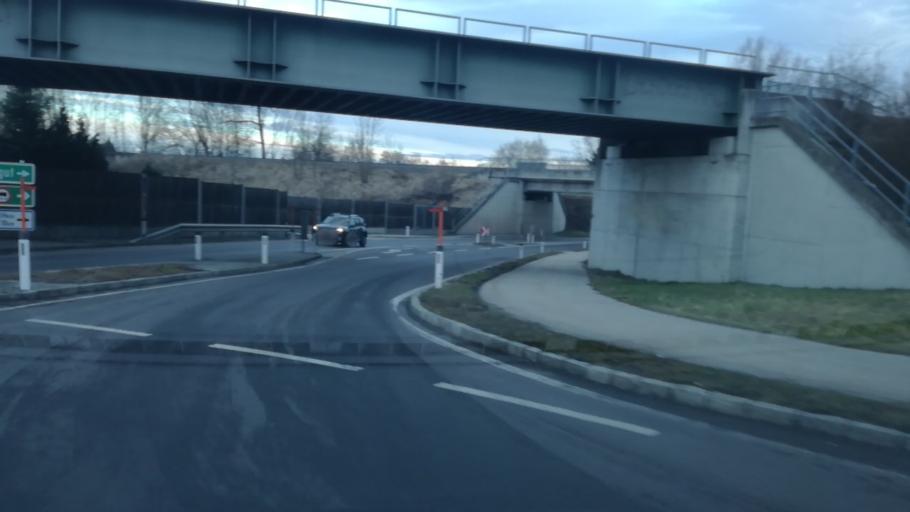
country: AT
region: Upper Austria
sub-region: Politischer Bezirk Ried im Innkreis
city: Ried im Innkreis
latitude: 48.2002
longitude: 13.4796
